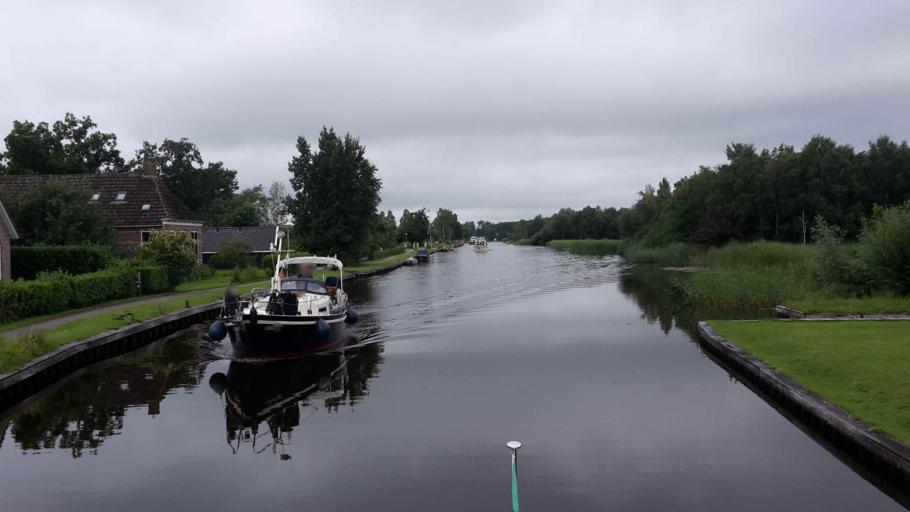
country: NL
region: Overijssel
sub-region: Gemeente Steenwijkerland
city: Oldemarkt
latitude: 52.7985
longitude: 5.9298
